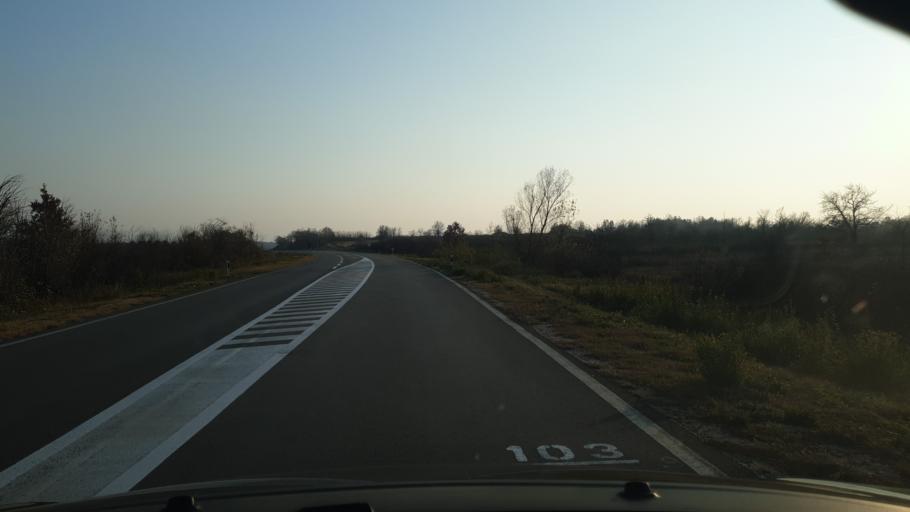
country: RS
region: Central Serbia
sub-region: Zajecarski Okrug
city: Zajecar
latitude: 44.0019
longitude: 22.3015
